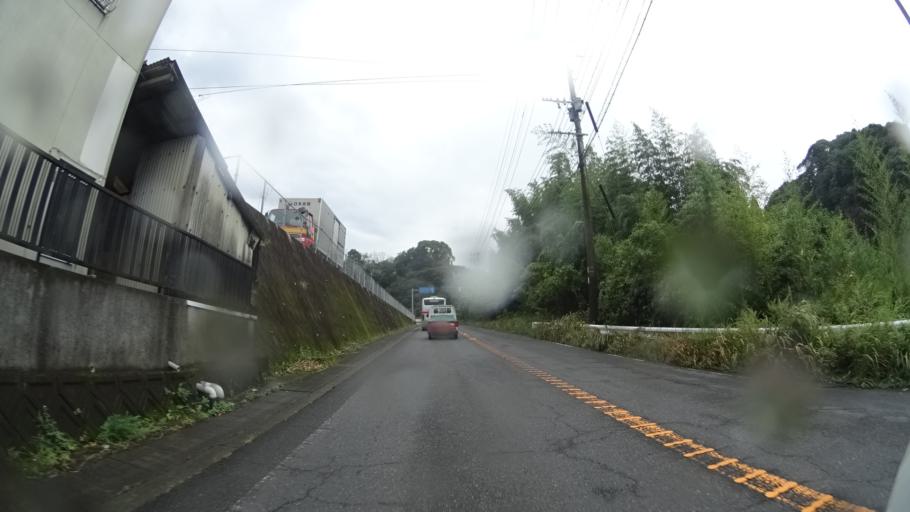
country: JP
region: Kagoshima
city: Kajiki
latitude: 31.7731
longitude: 130.6696
